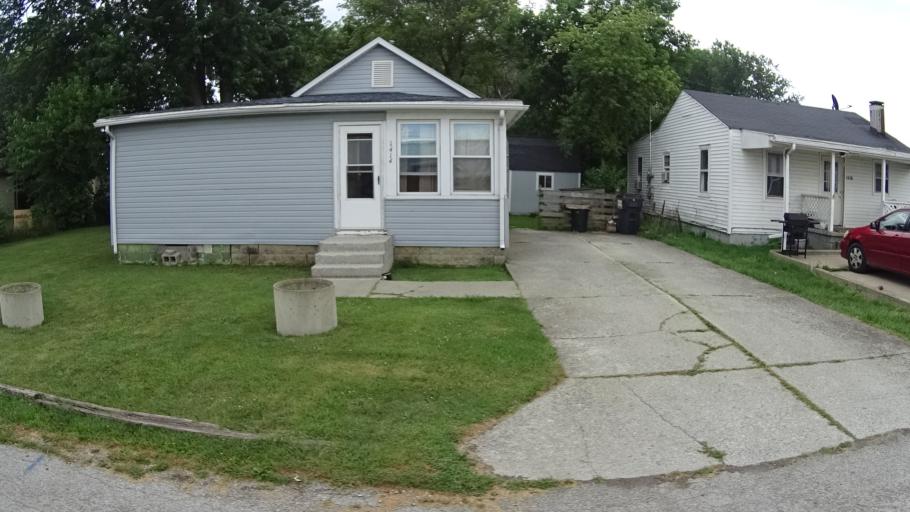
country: US
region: Ohio
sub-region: Erie County
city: Sandusky
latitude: 41.4402
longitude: -82.7521
